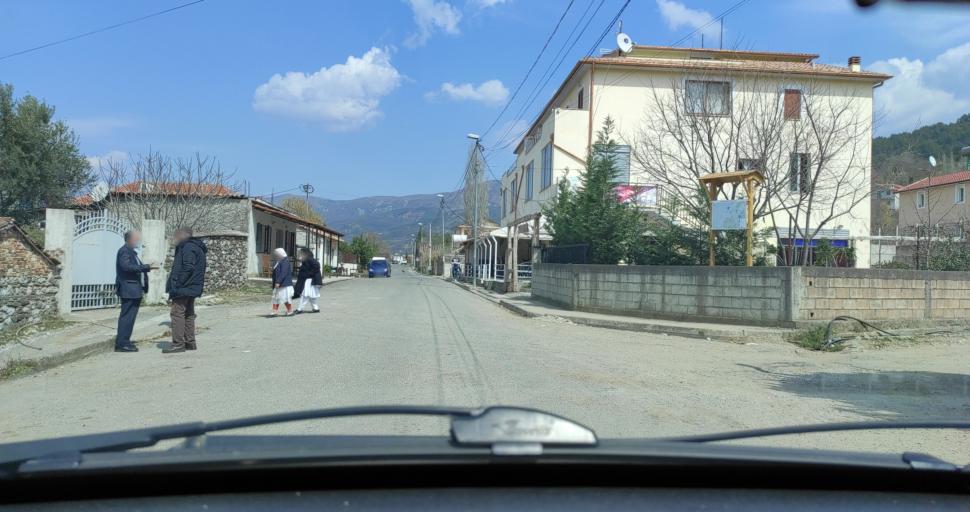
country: AL
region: Lezhe
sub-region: Rrethi i Lezhes
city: Kallmeti i Madh
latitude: 41.8489
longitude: 19.6903
